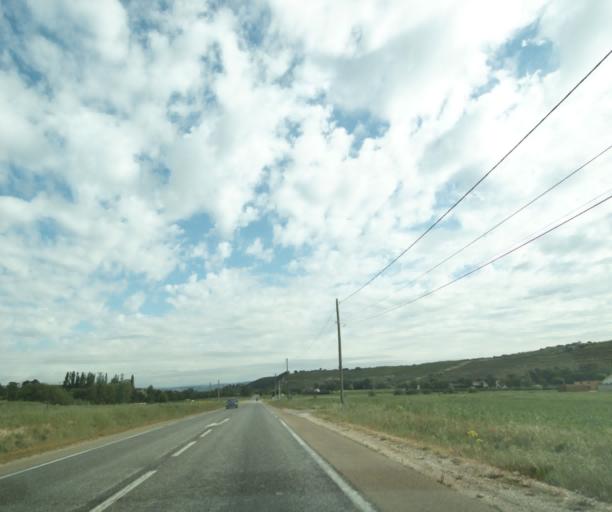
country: FR
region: Provence-Alpes-Cote d'Azur
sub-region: Departement des Bouches-du-Rhone
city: Cabries
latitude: 43.4709
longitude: 5.3547
